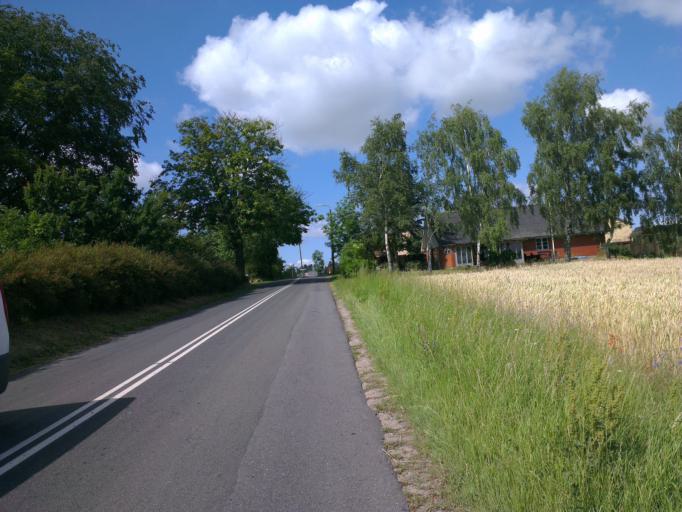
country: DK
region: Zealand
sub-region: Lejre Kommune
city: Ejby
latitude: 55.7421
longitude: 11.8817
